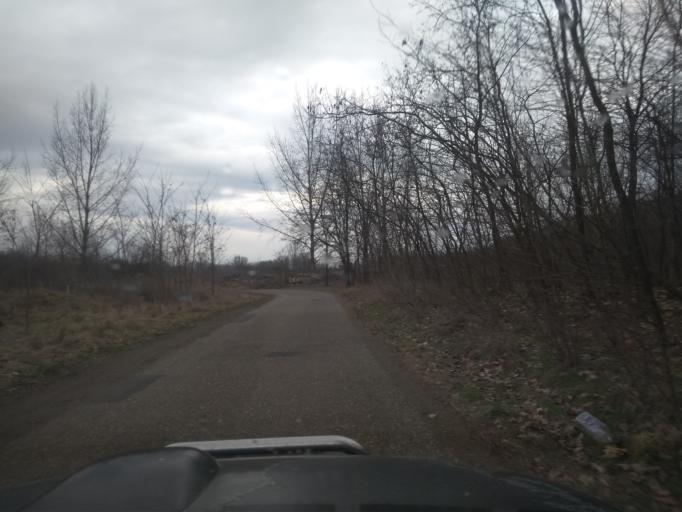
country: HU
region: Szabolcs-Szatmar-Bereg
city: Nyirpazony
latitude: 48.0141
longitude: 21.8105
